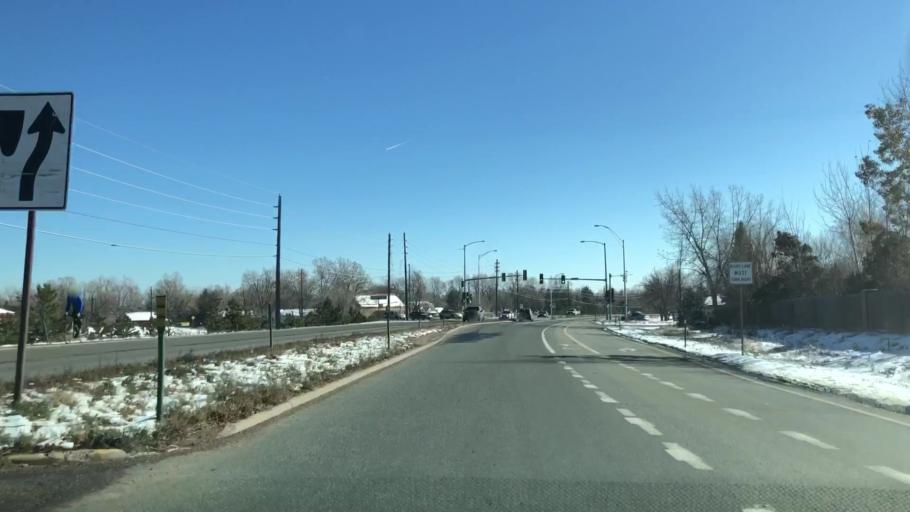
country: US
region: Colorado
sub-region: Boulder County
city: Boulder
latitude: 40.0519
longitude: -105.2610
